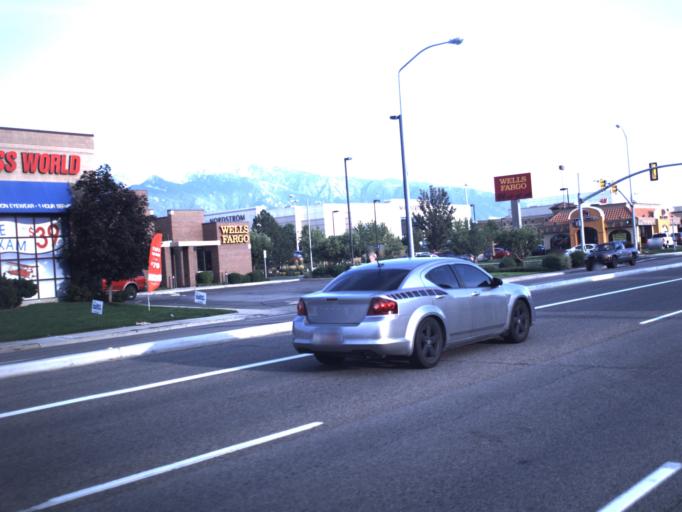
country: US
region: Utah
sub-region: Salt Lake County
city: Murray
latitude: 40.6392
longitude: -111.8893
